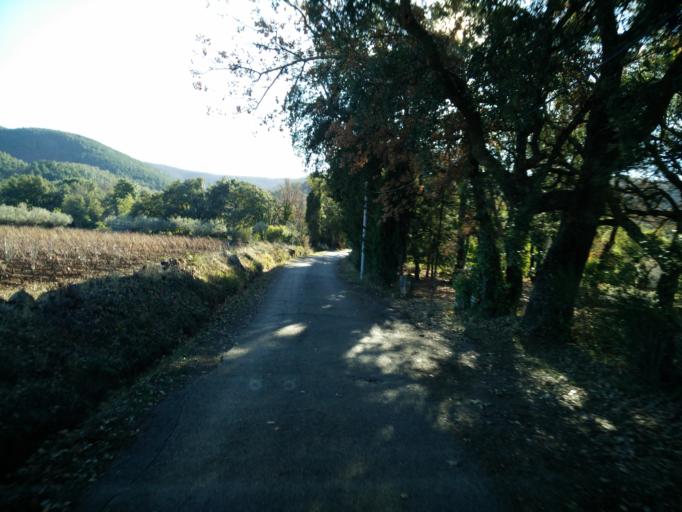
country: FR
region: Provence-Alpes-Cote d'Azur
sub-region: Departement du Var
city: Gonfaron
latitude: 43.3072
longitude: 6.2906
